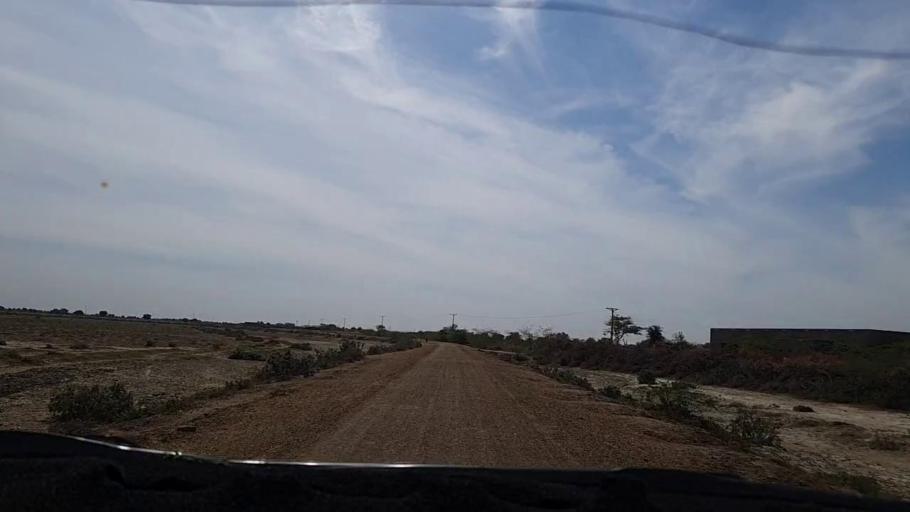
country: PK
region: Sindh
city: Pithoro
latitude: 25.4959
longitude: 69.4571
